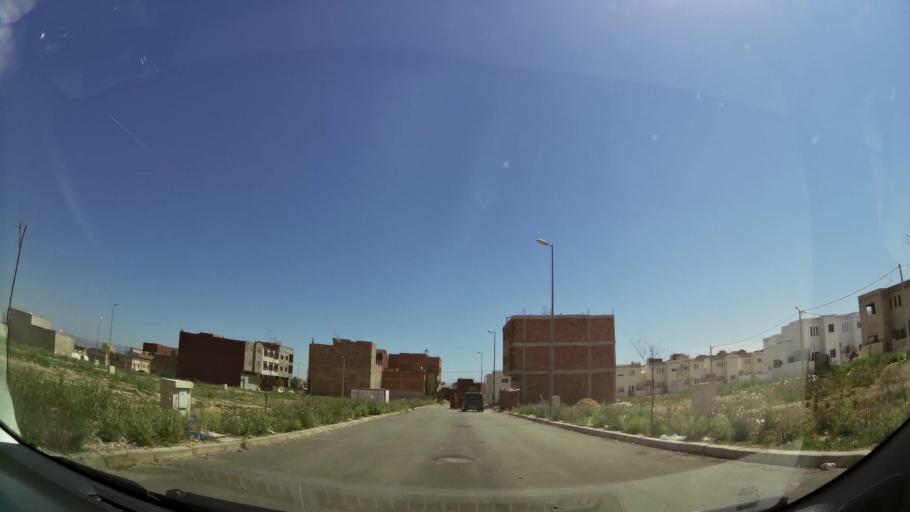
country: MA
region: Oriental
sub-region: Oujda-Angad
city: Oujda
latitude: 34.6524
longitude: -1.8768
